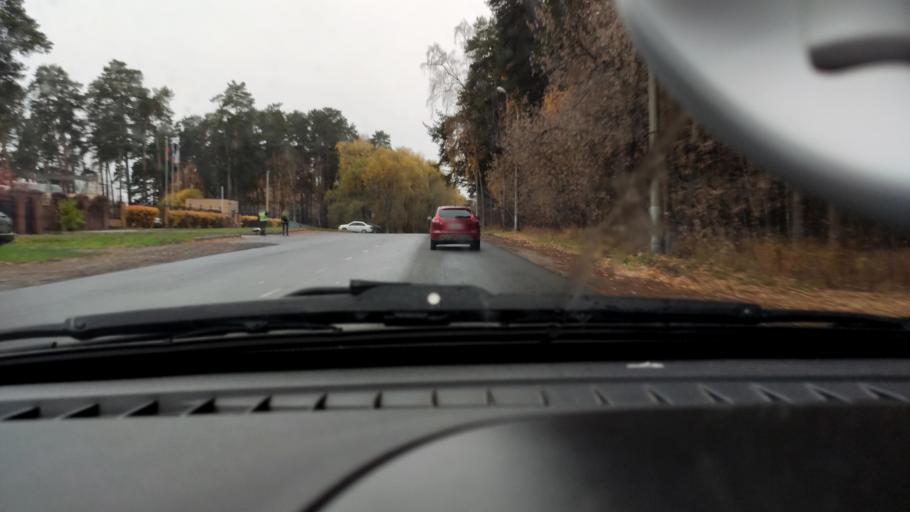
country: RU
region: Perm
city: Kultayevo
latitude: 58.0103
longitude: 55.9795
